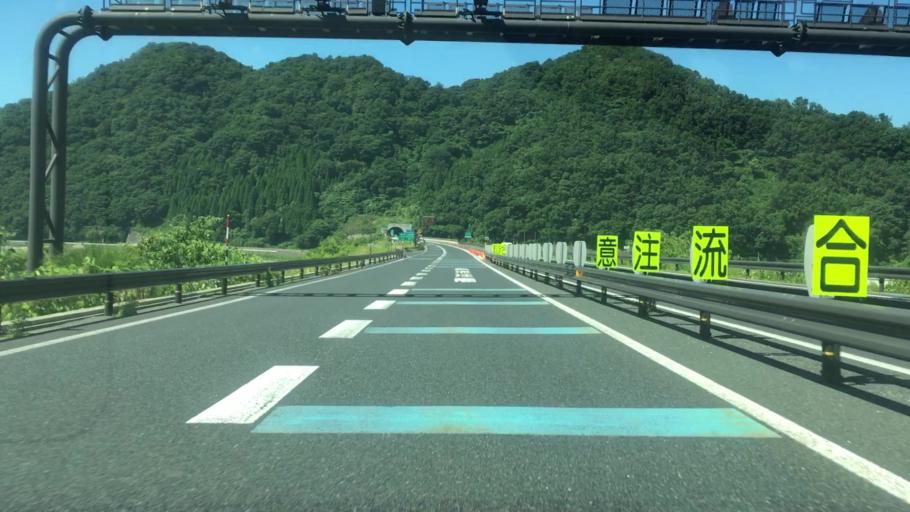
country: JP
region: Tottori
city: Tottori
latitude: 35.3763
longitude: 134.2044
